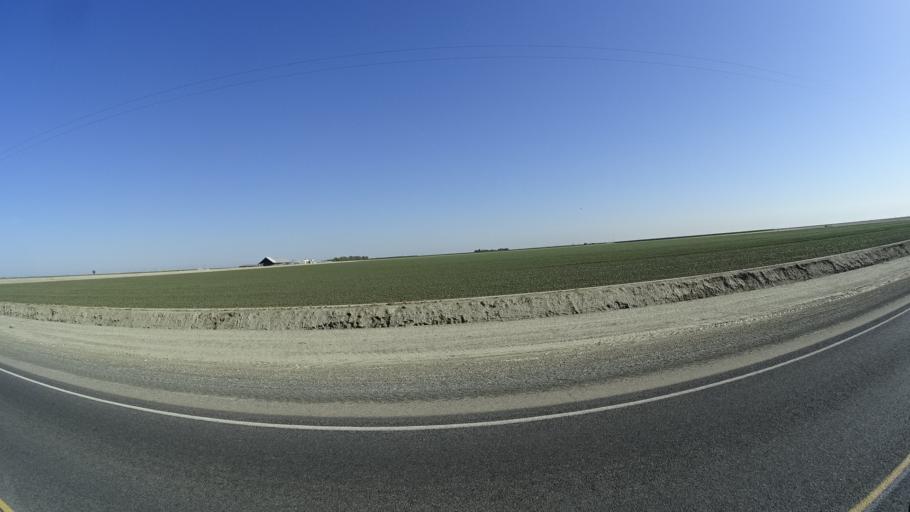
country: US
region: California
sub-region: Kings County
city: Corcoran
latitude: 36.0979
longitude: -119.6316
